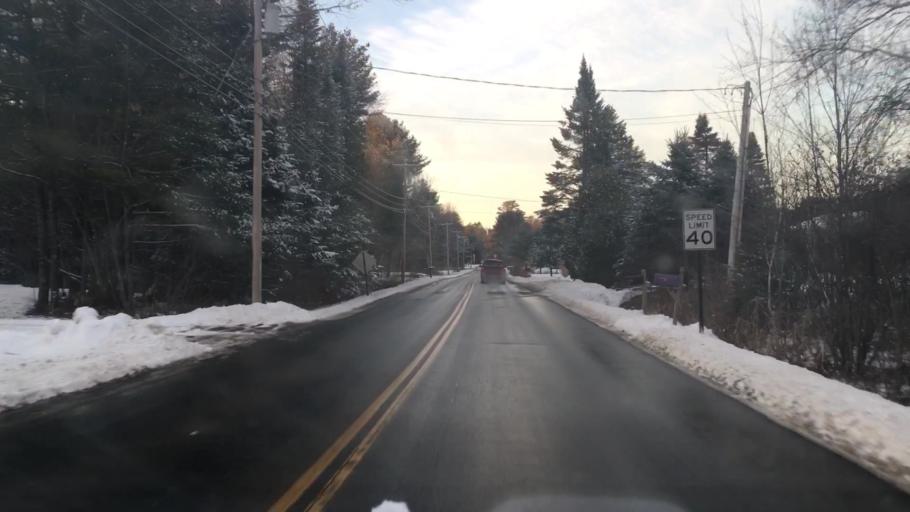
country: US
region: Maine
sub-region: Cumberland County
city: Brunswick
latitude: 43.9477
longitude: -69.9283
